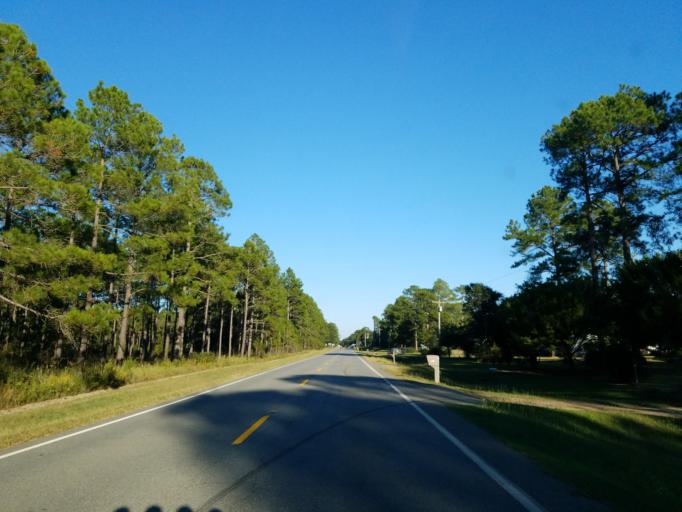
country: US
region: Georgia
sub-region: Lee County
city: Leesburg
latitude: 31.7269
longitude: -84.0518
